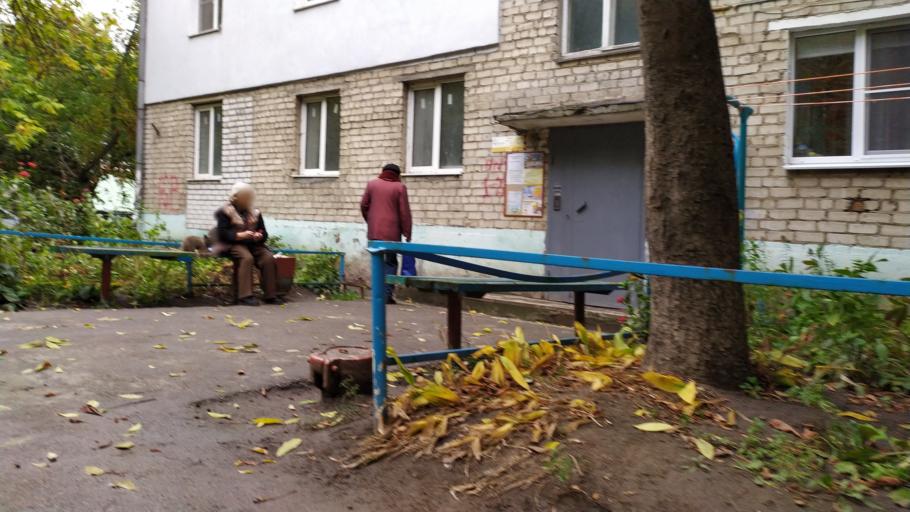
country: RU
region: Kursk
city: Kursk
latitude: 51.6509
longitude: 36.1386
